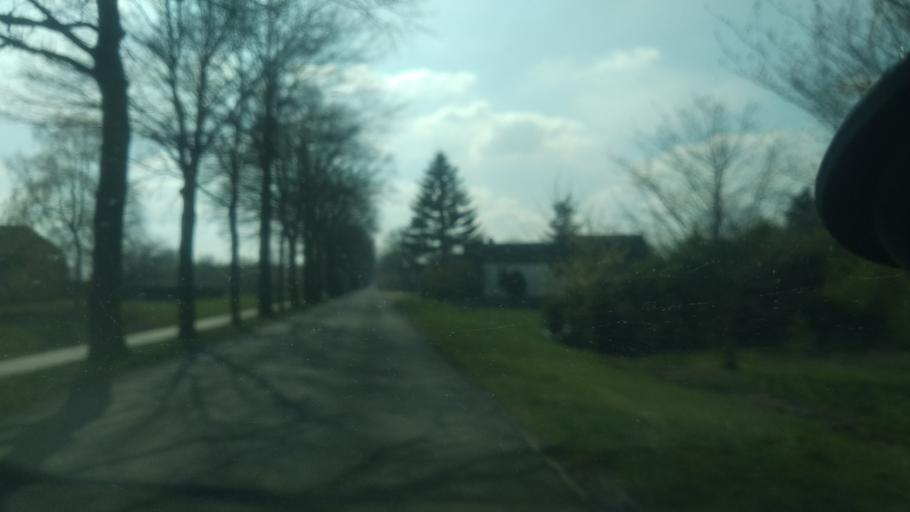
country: NL
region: Groningen
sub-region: Gemeente Stadskanaal
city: Stadskanaal
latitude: 52.9757
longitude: 6.8960
